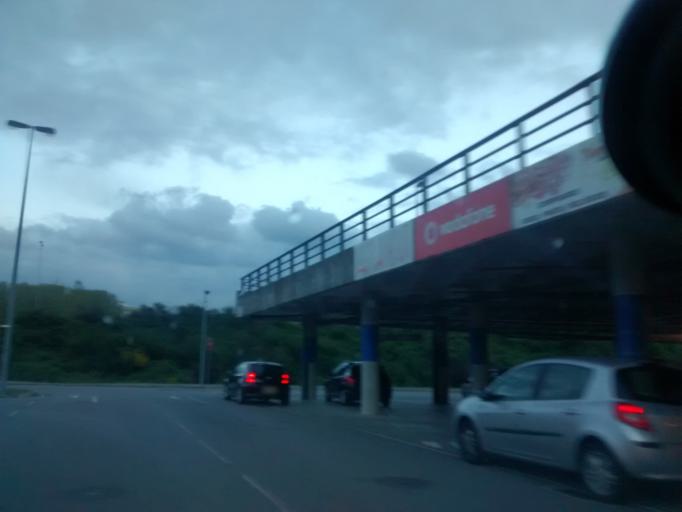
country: PT
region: Braga
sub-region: Braga
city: Braga
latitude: 41.5338
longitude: -8.4470
